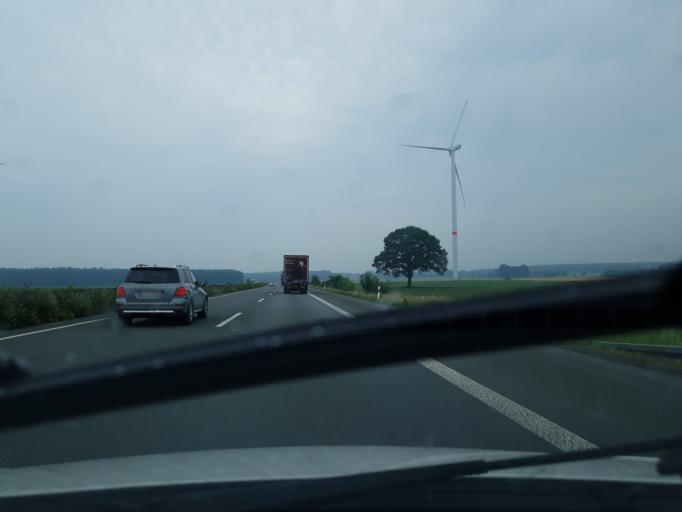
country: DE
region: North Rhine-Westphalia
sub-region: Regierungsbezirk Munster
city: Klein Reken
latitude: 51.8292
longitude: 7.0004
